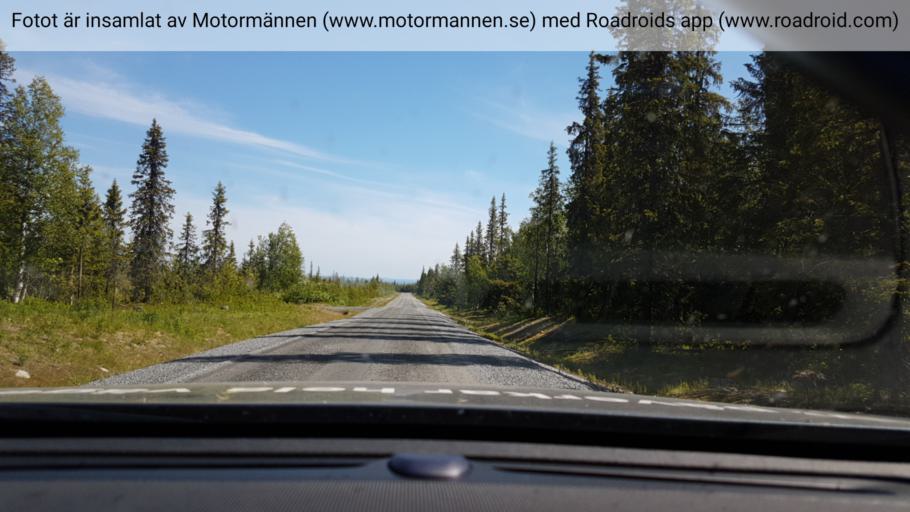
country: SE
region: Vaesterbotten
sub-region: Vilhelmina Kommun
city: Sjoberg
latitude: 64.7710
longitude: 15.9247
